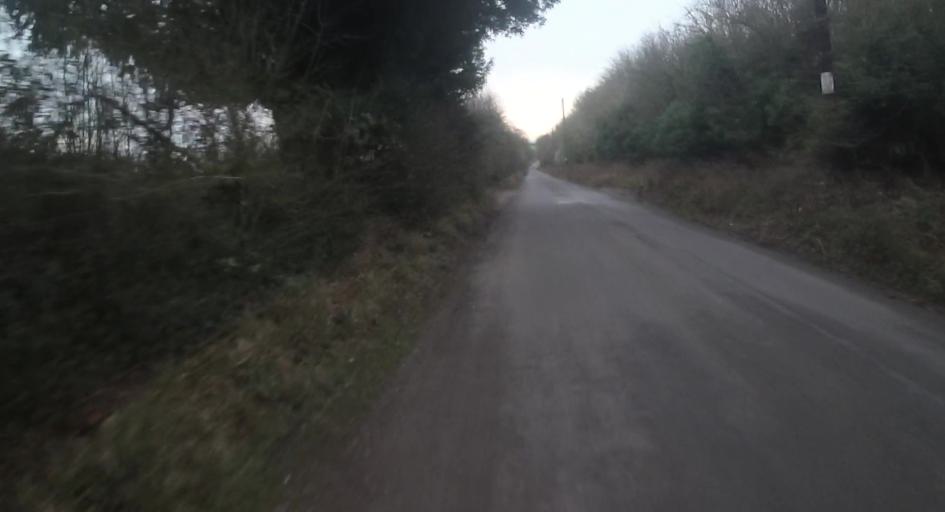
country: GB
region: England
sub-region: Hampshire
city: Andover
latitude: 51.1856
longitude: -1.3760
